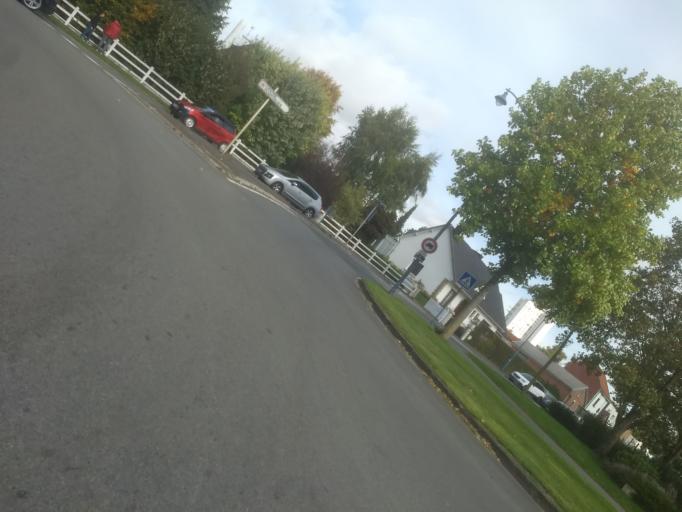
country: FR
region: Nord-Pas-de-Calais
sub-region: Departement du Pas-de-Calais
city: Achicourt
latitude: 50.2872
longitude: 2.7451
